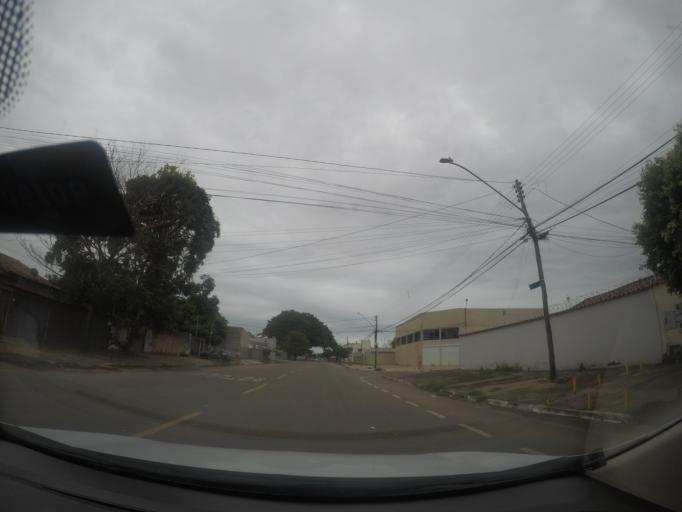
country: BR
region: Goias
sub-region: Goiania
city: Goiania
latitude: -16.6867
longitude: -49.3349
